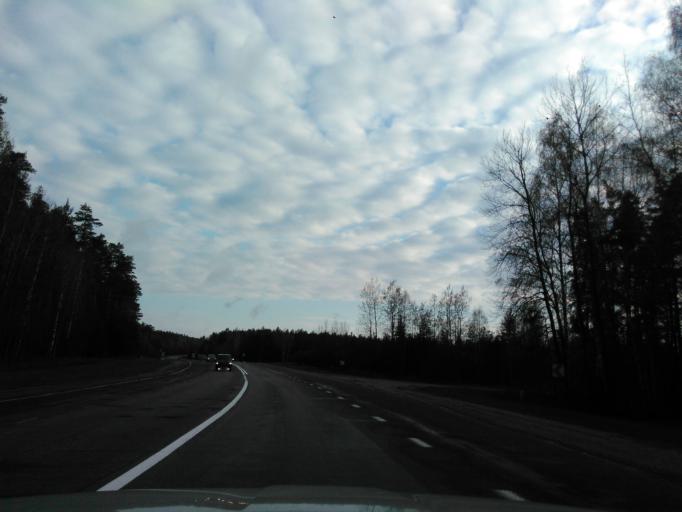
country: BY
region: Minsk
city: Plyeshchanitsy
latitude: 54.3503
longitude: 27.8798
